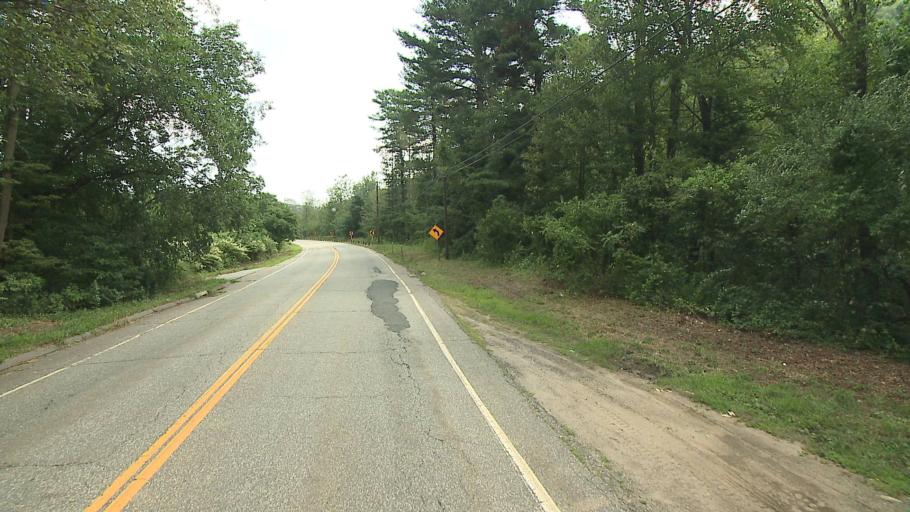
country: US
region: Connecticut
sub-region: Litchfield County
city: Oakville
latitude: 41.6241
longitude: -73.0667
